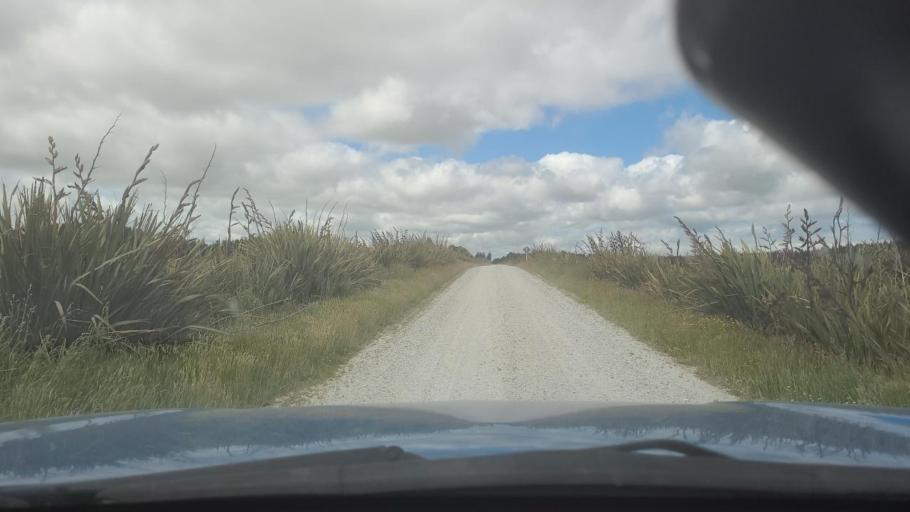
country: NZ
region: Southland
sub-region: Invercargill City
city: Invercargill
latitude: -46.4997
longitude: 168.5769
